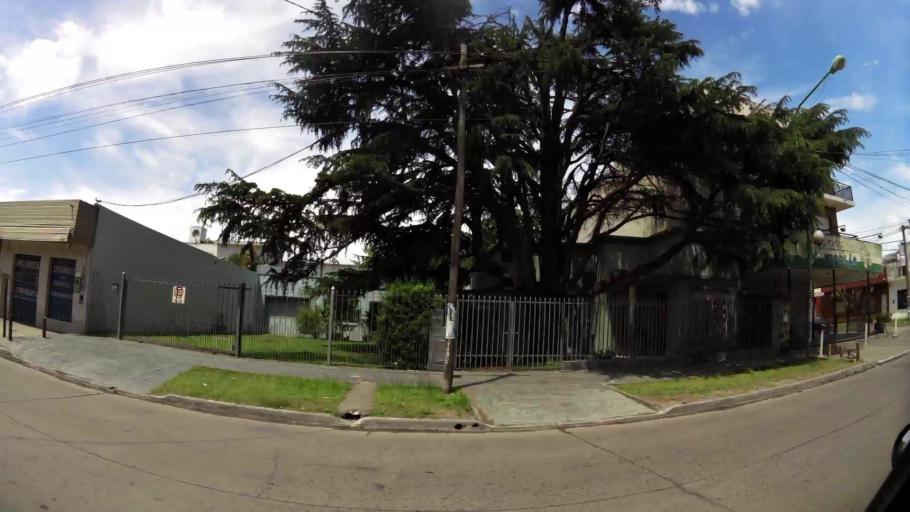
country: AR
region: Buenos Aires
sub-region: Partido de Quilmes
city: Quilmes
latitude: -34.7832
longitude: -58.2668
